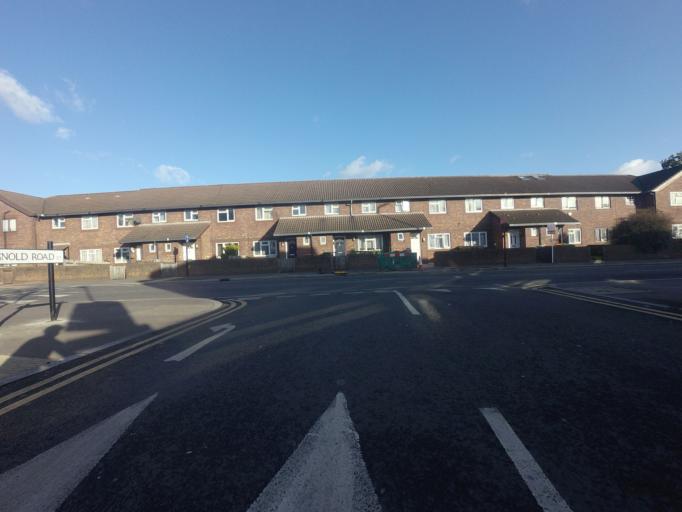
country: GB
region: England
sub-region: Greater London
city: East Ham
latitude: 51.5533
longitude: 0.0238
